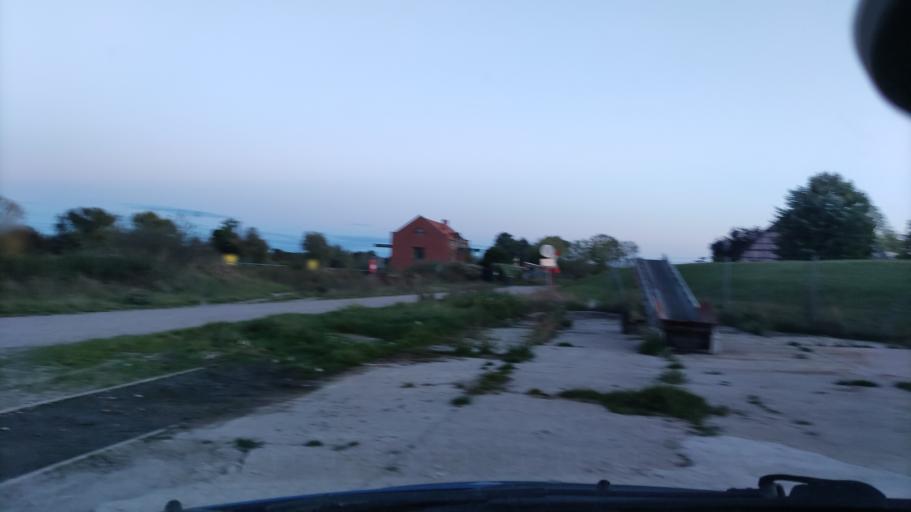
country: DE
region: Lower Saxony
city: Bleckede
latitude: 53.2927
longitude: 10.7362
